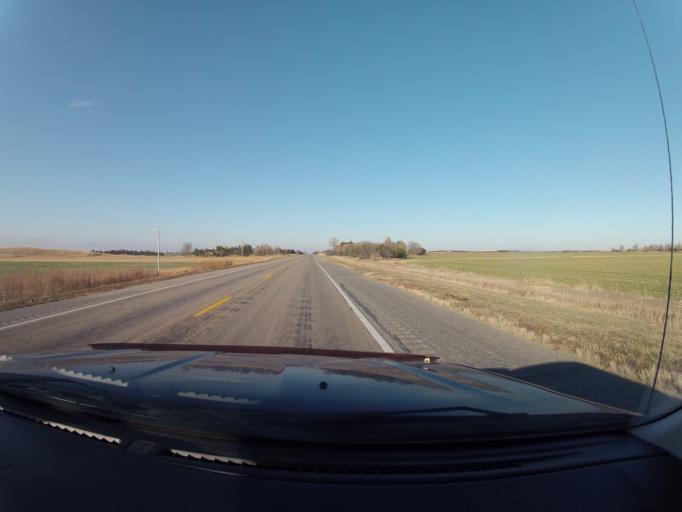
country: US
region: Nebraska
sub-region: Kearney County
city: Minden
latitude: 40.5924
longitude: -98.9517
